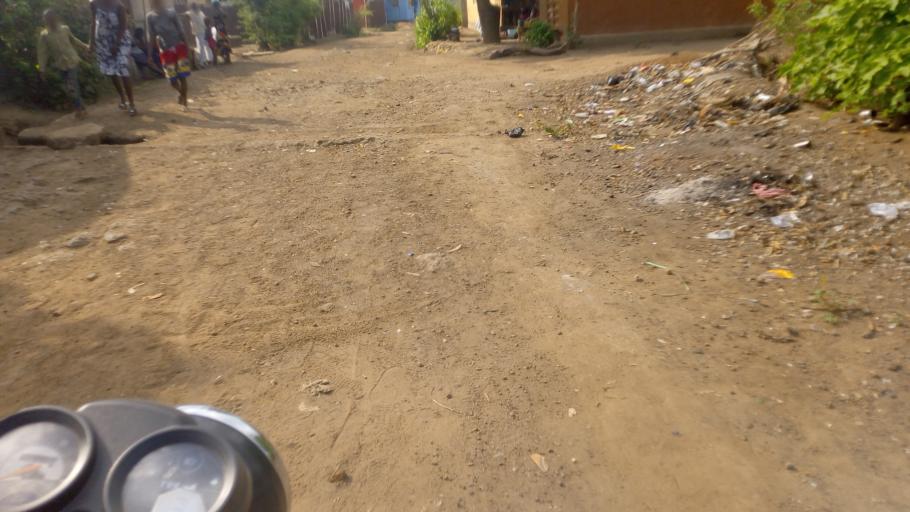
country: SL
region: Western Area
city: Waterloo
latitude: 8.3228
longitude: -13.0774
